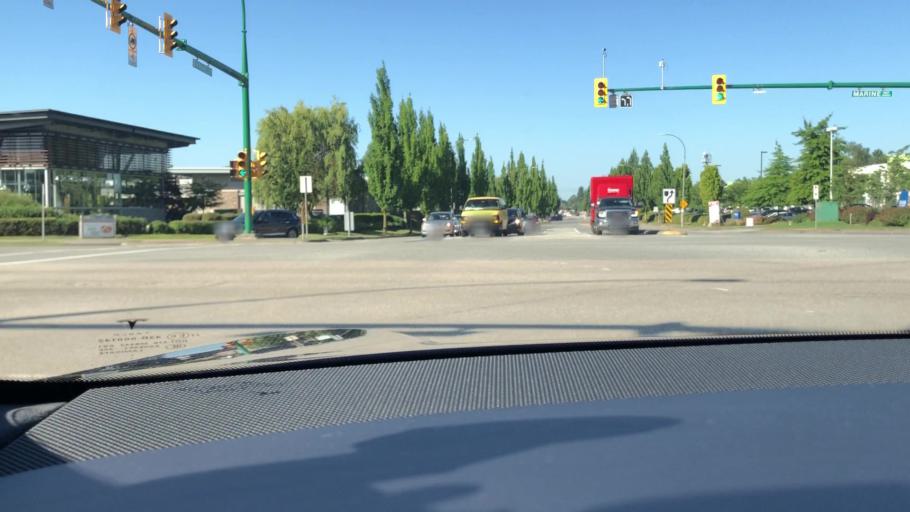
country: CA
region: British Columbia
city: Burnaby
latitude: 49.2021
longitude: -122.9818
